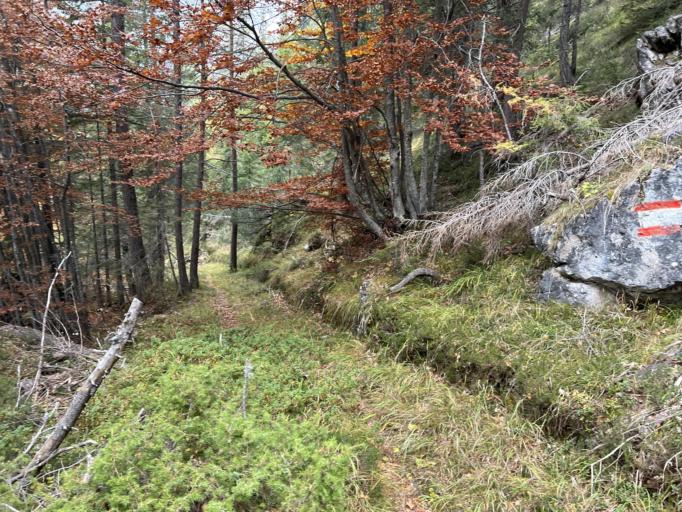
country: IT
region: Veneto
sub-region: Provincia di Belluno
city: San Pietro di Cadore
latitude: 46.5847
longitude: 12.6345
